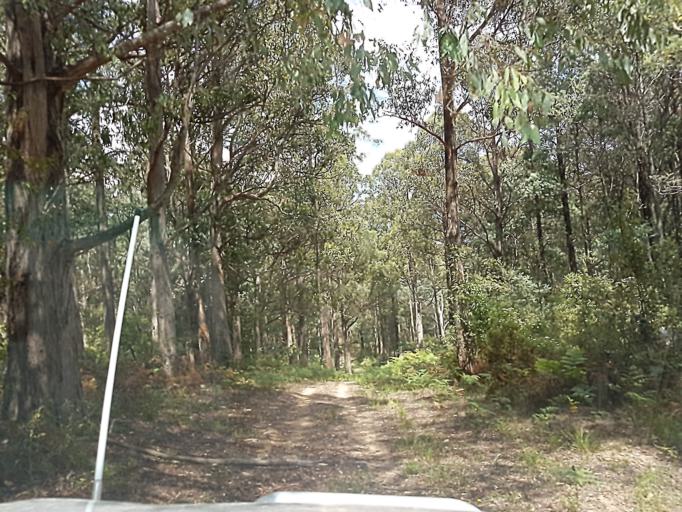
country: AU
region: Victoria
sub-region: East Gippsland
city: Lakes Entrance
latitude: -37.3300
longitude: 148.3220
